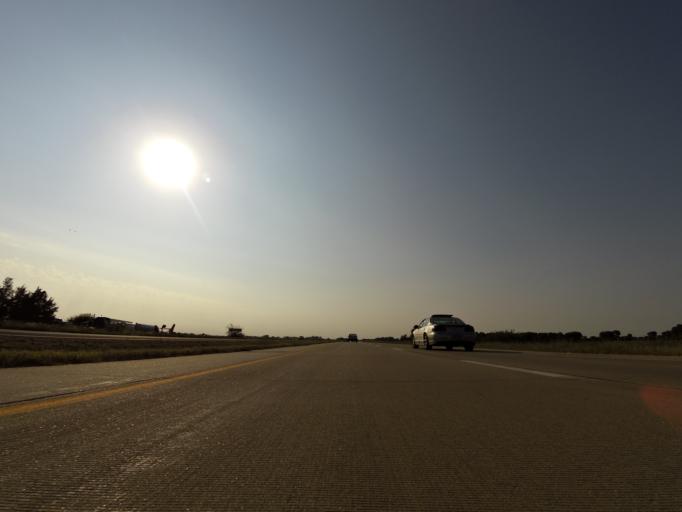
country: US
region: Kansas
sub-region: Sedgwick County
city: Colwich
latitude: 37.8478
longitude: -97.5925
